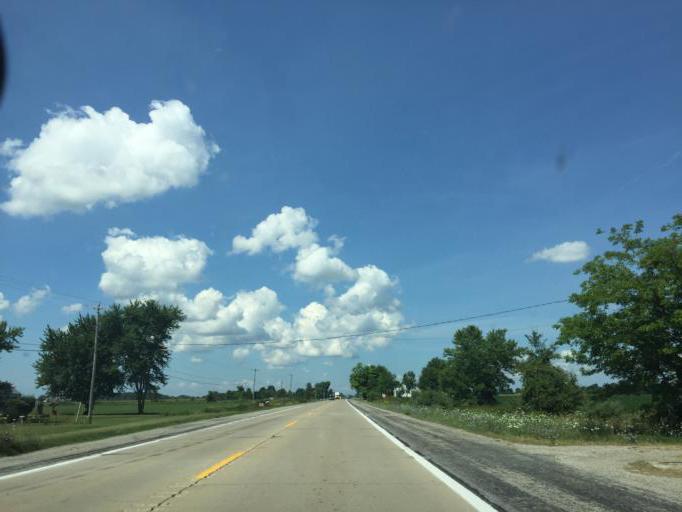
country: US
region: Ohio
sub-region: Lucas County
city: Sylvania
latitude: 41.7967
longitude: -83.7202
